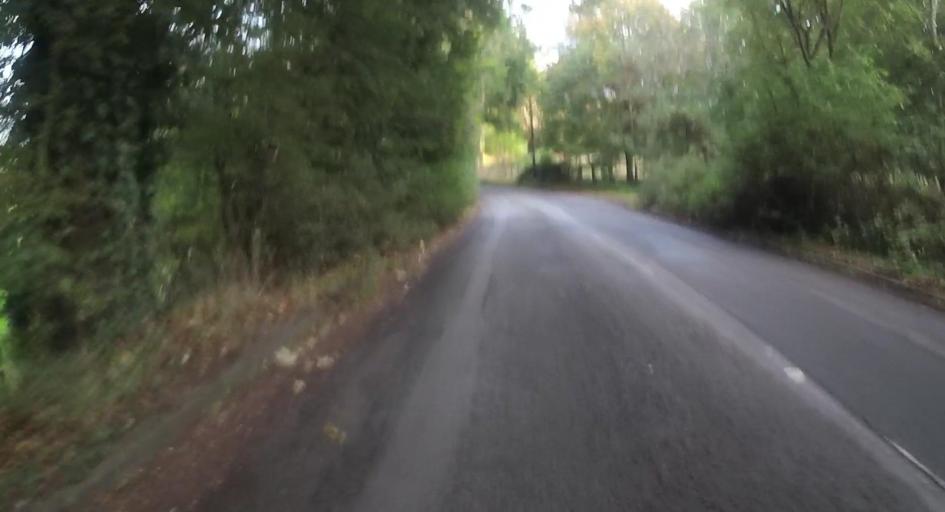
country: GB
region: England
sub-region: Hampshire
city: Tadley
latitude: 51.3808
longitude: -1.1379
